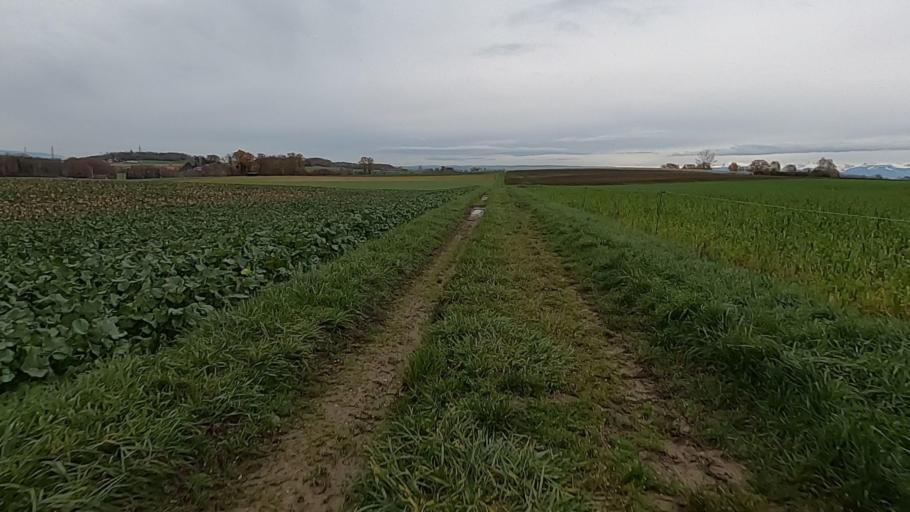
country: CH
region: Vaud
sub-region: Morges District
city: Apples
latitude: 46.5256
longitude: 6.4507
